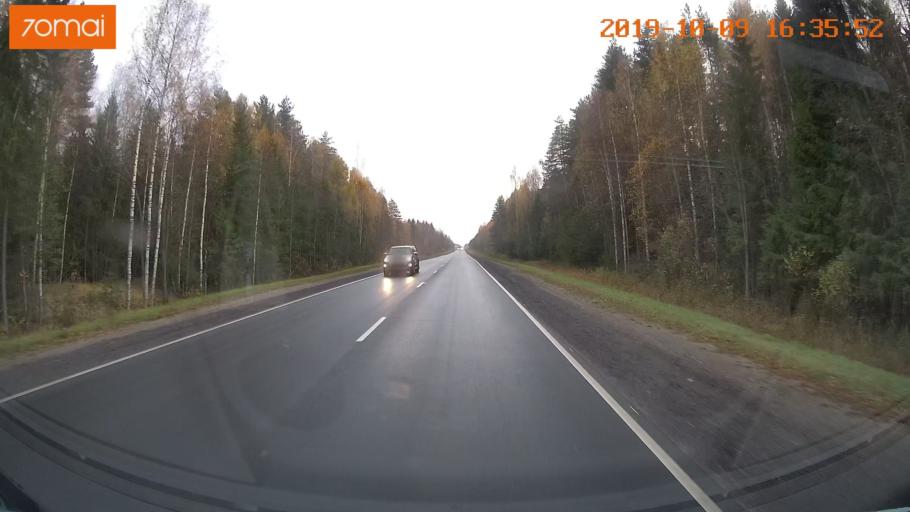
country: RU
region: Kostroma
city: Volgorechensk
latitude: 57.5496
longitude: 41.0059
